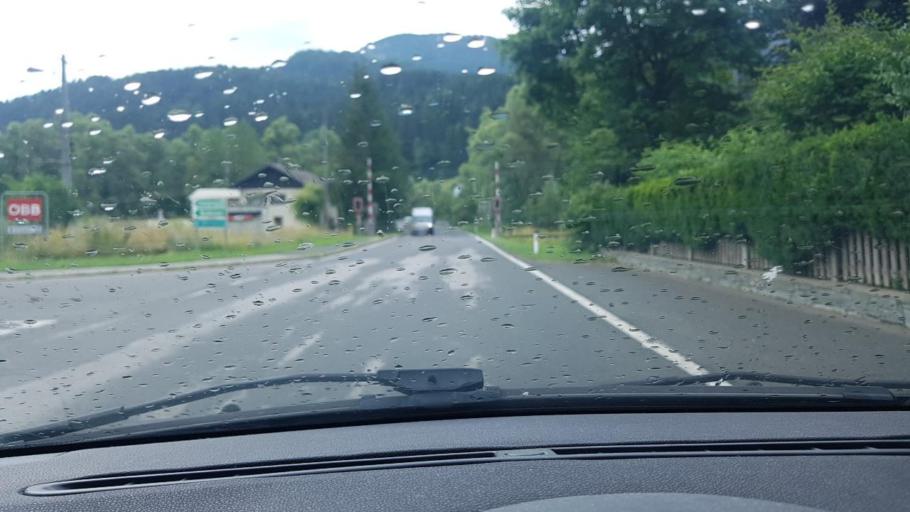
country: AT
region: Carinthia
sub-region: Politischer Bezirk Spittal an der Drau
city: Greifenburg
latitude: 46.7403
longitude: 13.1878
